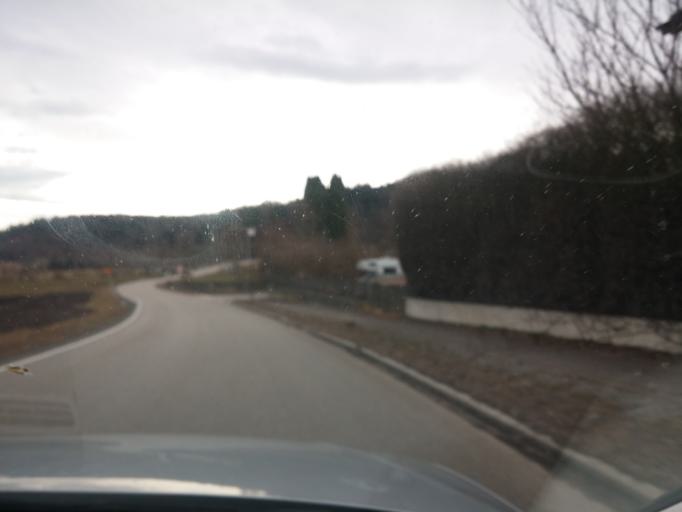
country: DE
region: Bavaria
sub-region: Upper Bavaria
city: Moosach
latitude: 48.0299
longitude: 11.8740
